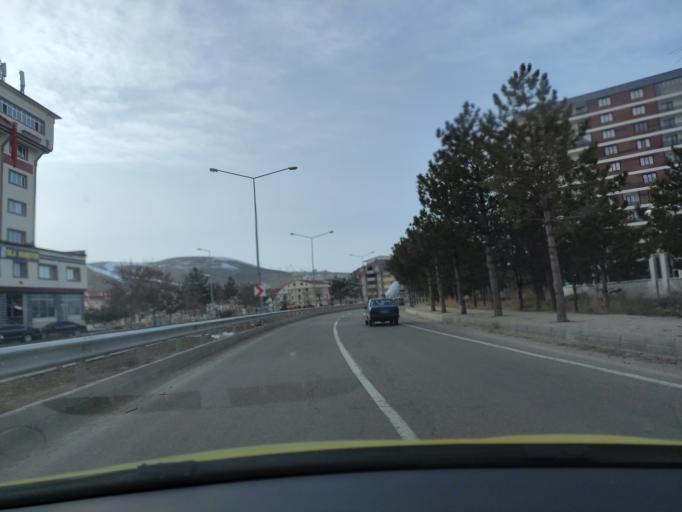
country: TR
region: Bayburt
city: Bayburt
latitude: 40.2447
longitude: 40.2357
